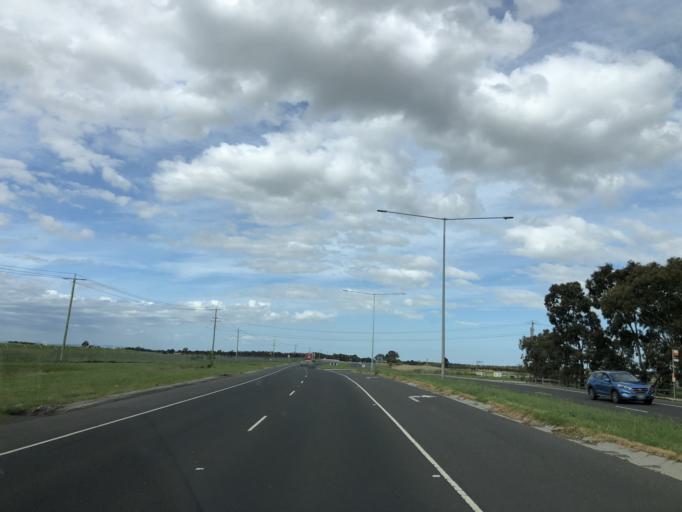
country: AU
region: Victoria
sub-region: Kingston
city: Patterson Lakes
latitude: -38.0672
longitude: 145.1550
